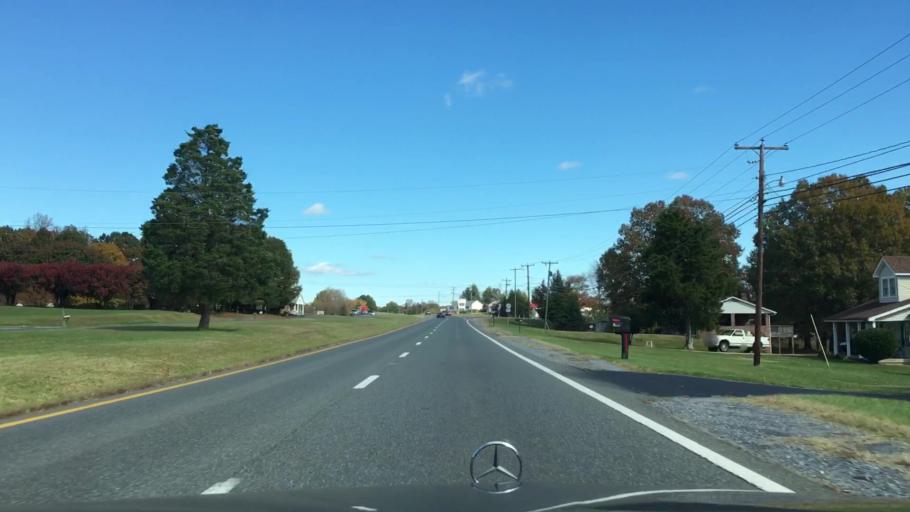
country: US
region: Virginia
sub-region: Campbell County
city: Altavista
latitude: 37.1672
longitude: -79.2125
